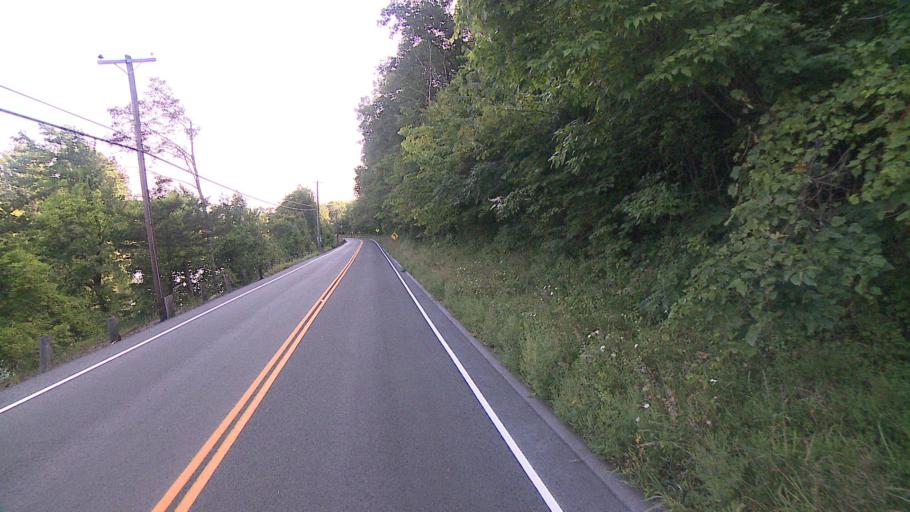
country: US
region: Connecticut
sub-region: Litchfield County
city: Kent
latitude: 41.7138
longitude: -73.4836
